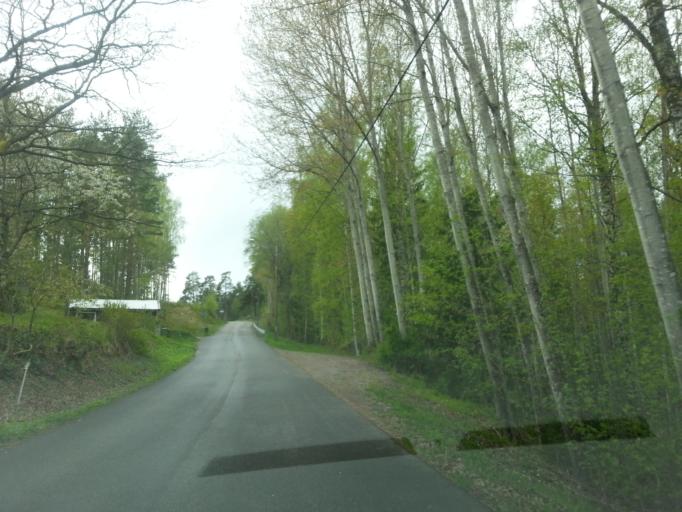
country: SE
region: OEstergoetland
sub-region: Norrkopings Kommun
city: Jursla
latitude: 58.6759
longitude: 16.2072
